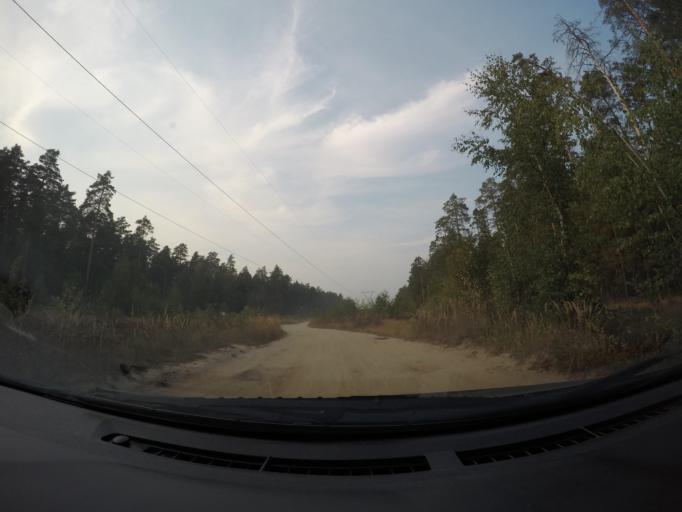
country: RU
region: Moskovskaya
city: Imeni Tsyurupy
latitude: 55.4990
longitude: 38.6880
